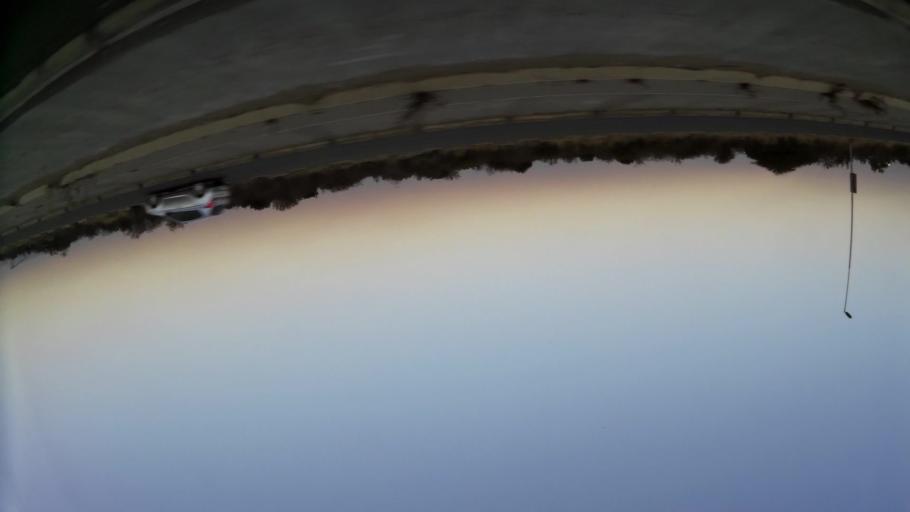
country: ZA
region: North-West
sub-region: Bojanala Platinum District Municipality
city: Rustenburg
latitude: -25.6412
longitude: 27.2626
